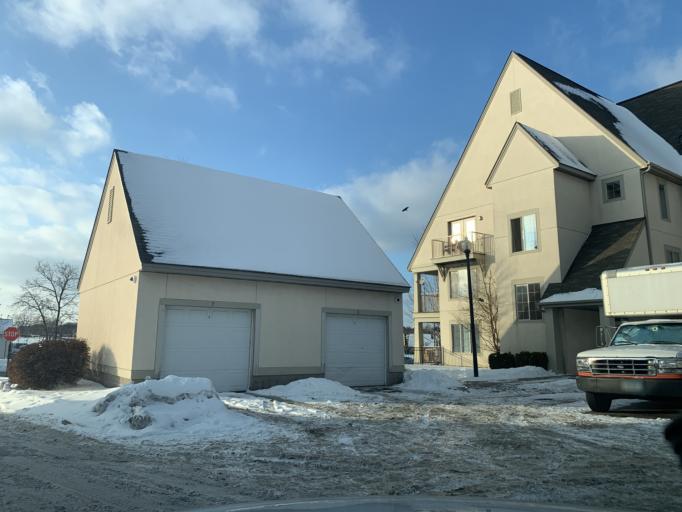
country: US
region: Minnesota
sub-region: Hennepin County
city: Minneapolis
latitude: 44.9837
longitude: -93.2904
